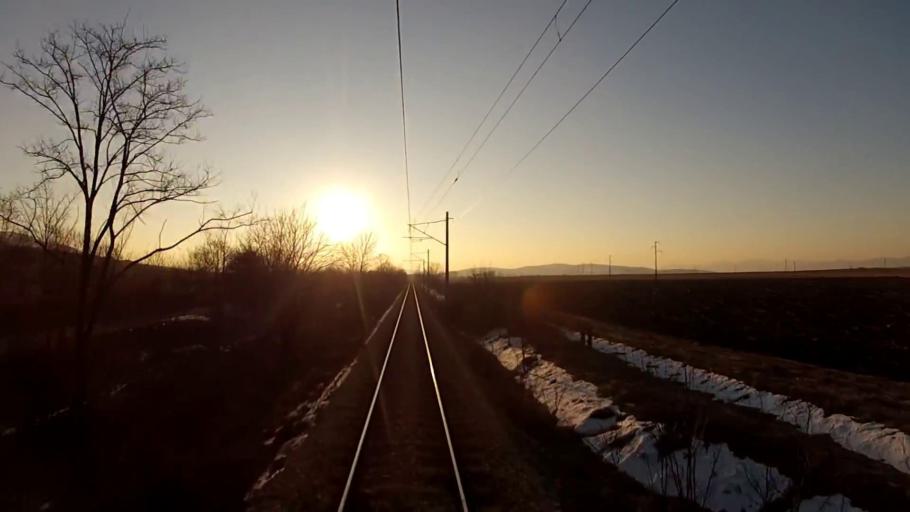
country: BG
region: Sofiya
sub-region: Obshtina Dragoman
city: Dragoman
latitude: 42.8917
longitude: 22.9733
